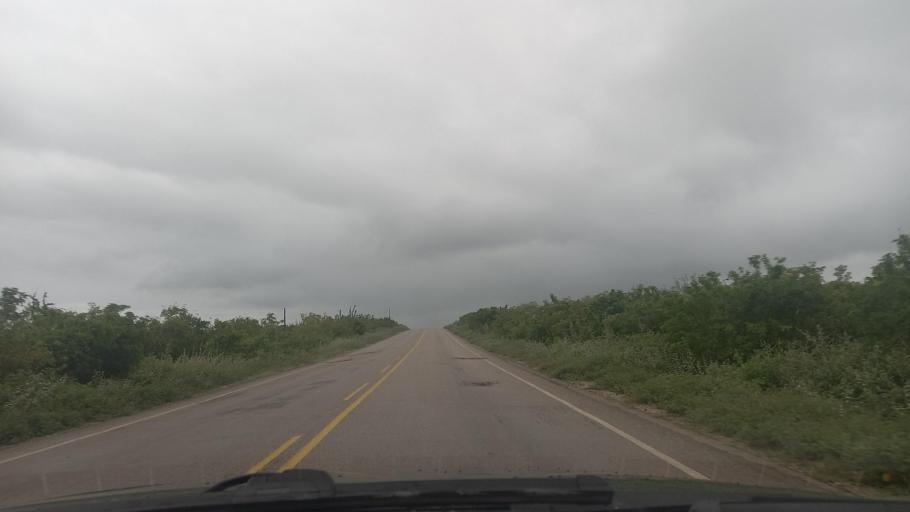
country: BR
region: Bahia
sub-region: Paulo Afonso
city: Paulo Afonso
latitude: -9.3215
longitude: -38.2899
